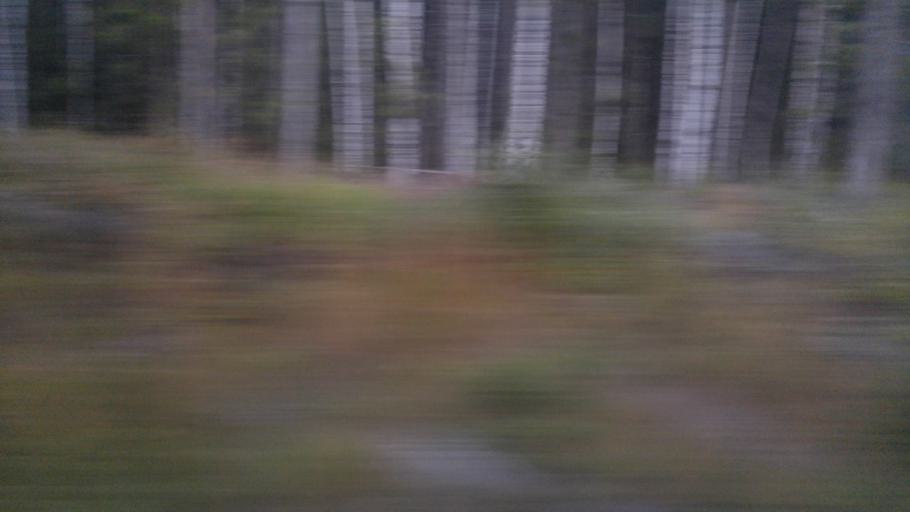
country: NO
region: Hedmark
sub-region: Stange
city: Stange
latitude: 60.6278
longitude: 11.2466
